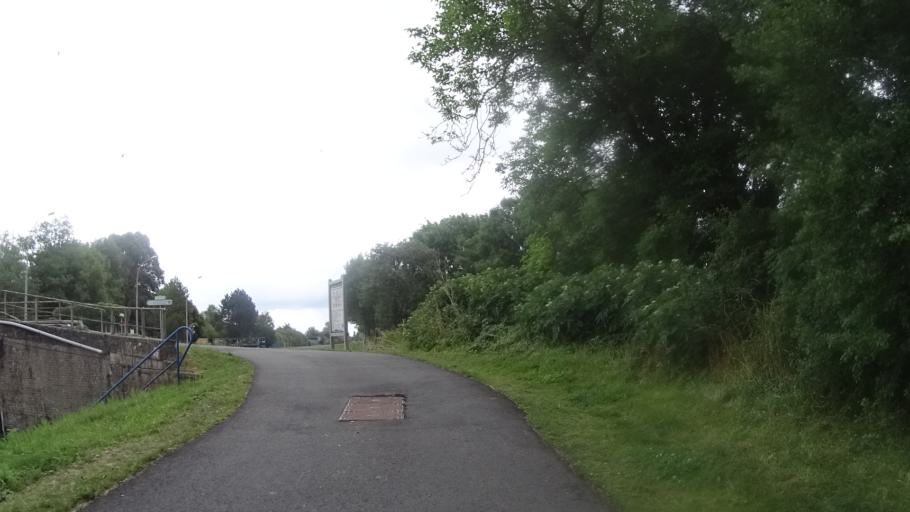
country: FR
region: Lorraine
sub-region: Departement de Meurthe-et-Moselle
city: Einville-au-Jard
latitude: 48.6781
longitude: 6.5720
